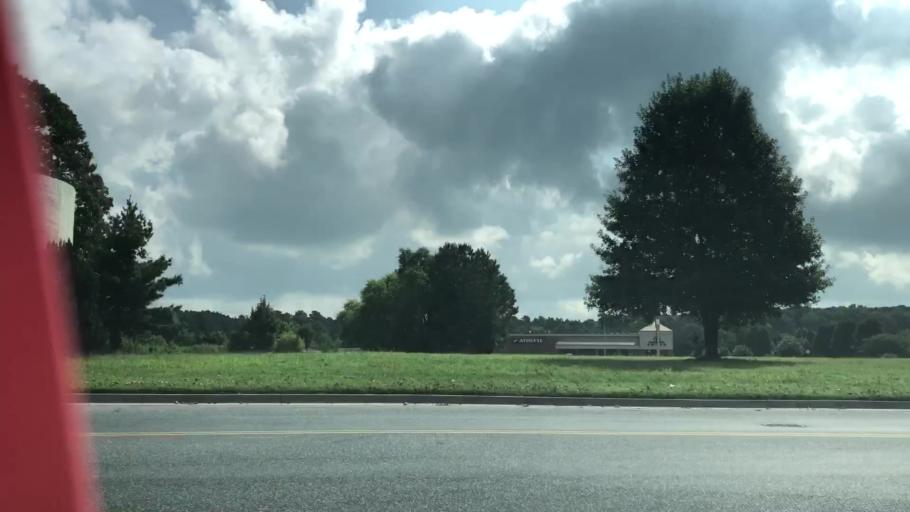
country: US
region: Maryland
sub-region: Wicomico County
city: Salisbury
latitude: 38.4015
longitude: -75.5647
